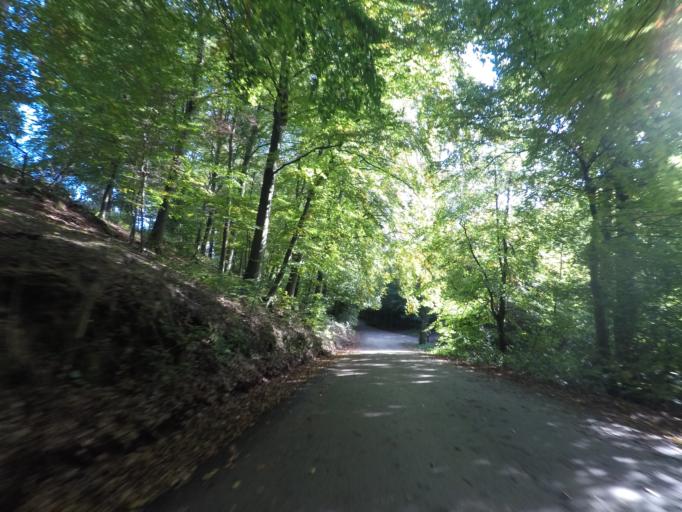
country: LU
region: Luxembourg
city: Itzig
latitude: 49.5954
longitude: 6.1737
